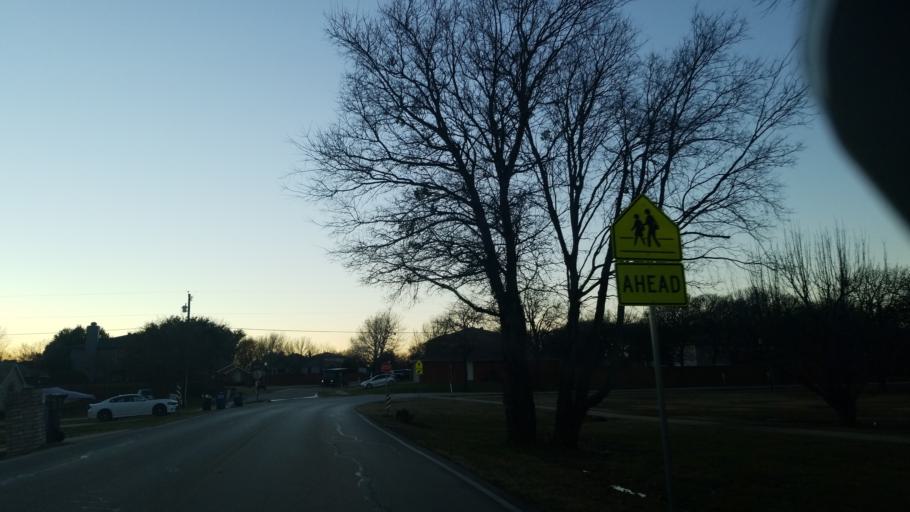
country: US
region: Texas
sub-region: Denton County
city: Hickory Creek
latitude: 33.1325
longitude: -97.0552
